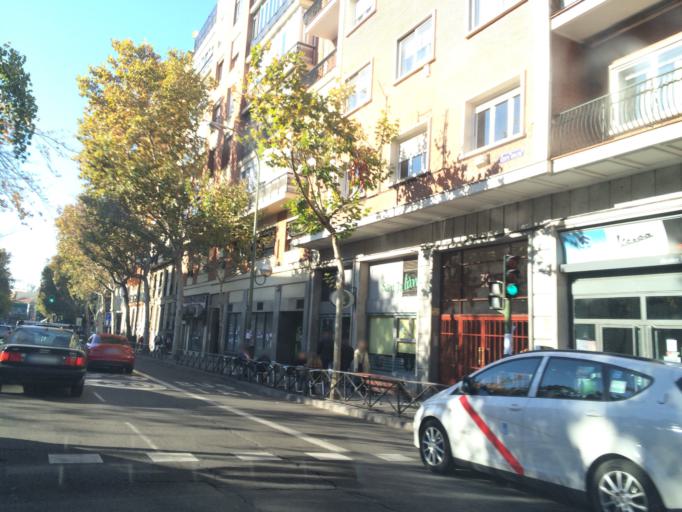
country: ES
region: Madrid
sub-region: Provincia de Madrid
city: Chamberi
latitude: 40.4301
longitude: -3.7105
